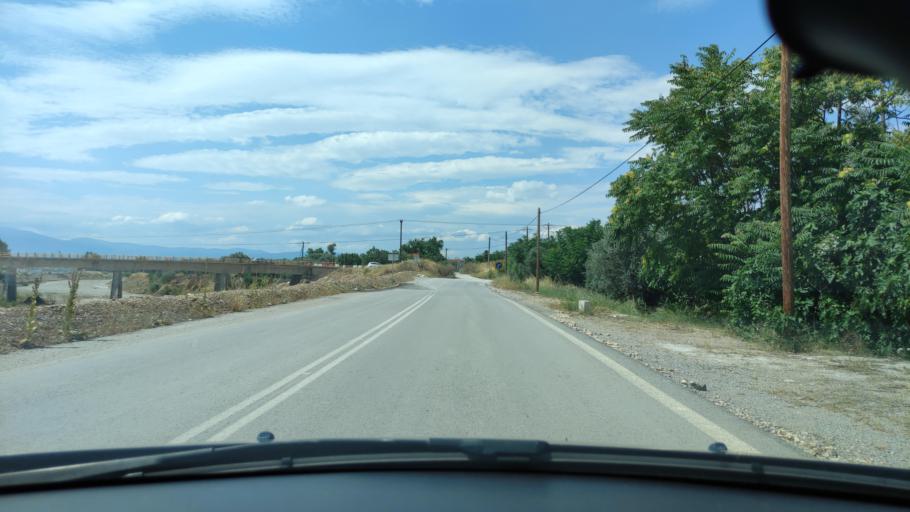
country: GR
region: Central Greece
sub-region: Nomos Evvoias
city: Vasilikon
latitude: 38.4301
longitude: 23.6616
